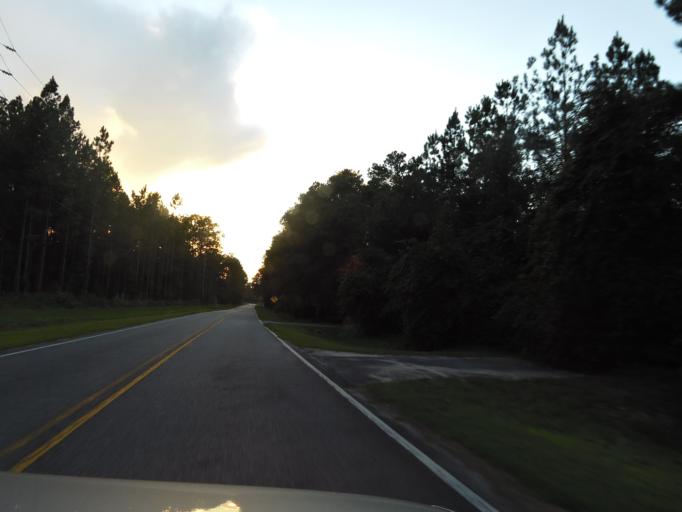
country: US
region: Georgia
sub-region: Camden County
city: Kingsland
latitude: 30.7737
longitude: -81.7021
